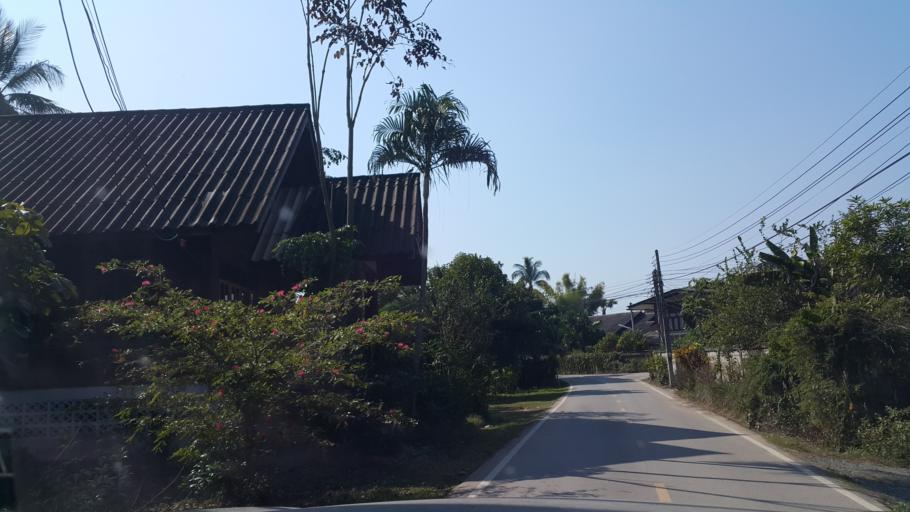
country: TH
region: Chiang Mai
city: Mae On
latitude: 18.7294
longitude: 99.2100
